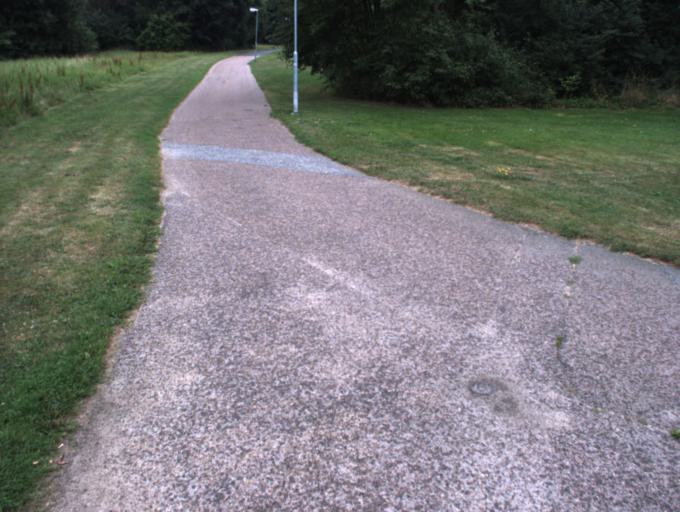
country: SE
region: Skane
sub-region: Helsingborg
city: Helsingborg
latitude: 56.0503
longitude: 12.7399
